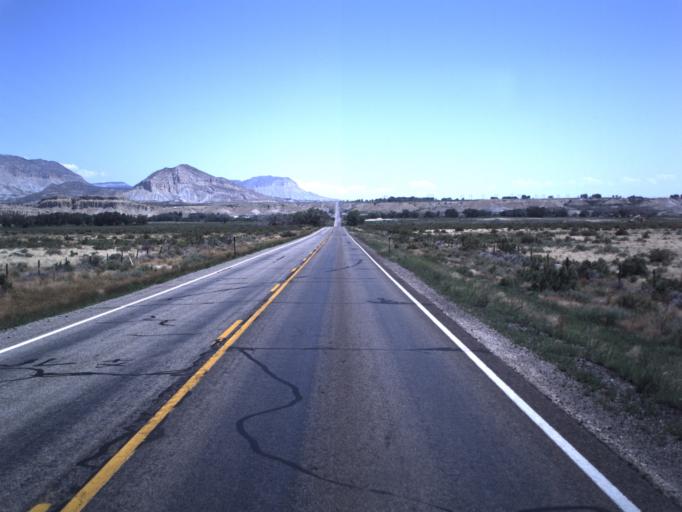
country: US
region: Utah
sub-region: Emery County
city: Ferron
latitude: 38.8589
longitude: -111.3025
